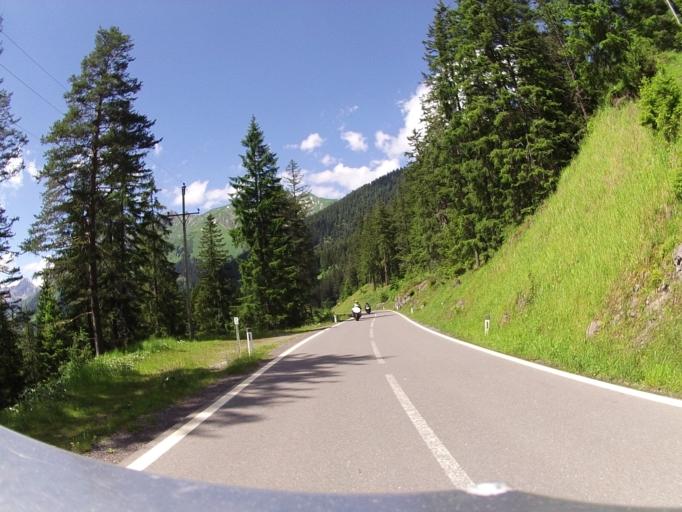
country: AT
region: Tyrol
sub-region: Politischer Bezirk Reutte
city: Gramais
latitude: 47.2964
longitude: 10.6021
